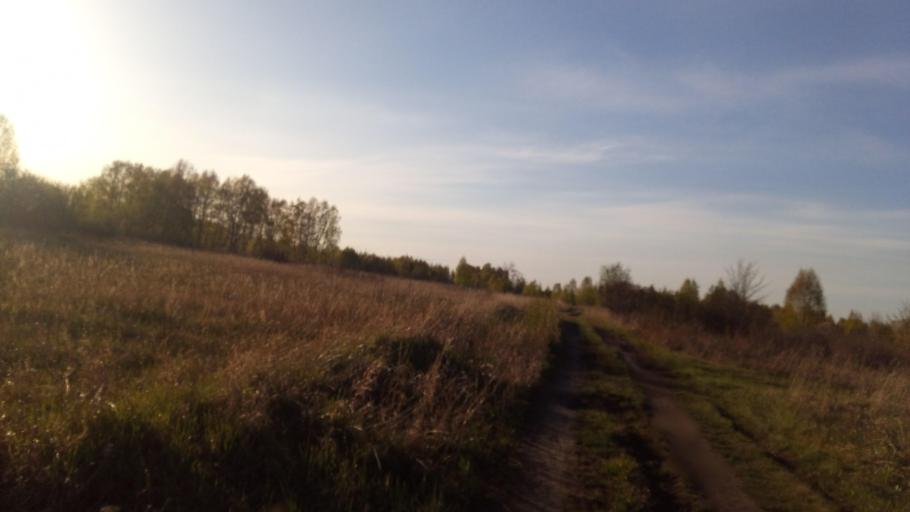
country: RU
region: Chelyabinsk
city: Timiryazevskiy
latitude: 54.9890
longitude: 60.8534
